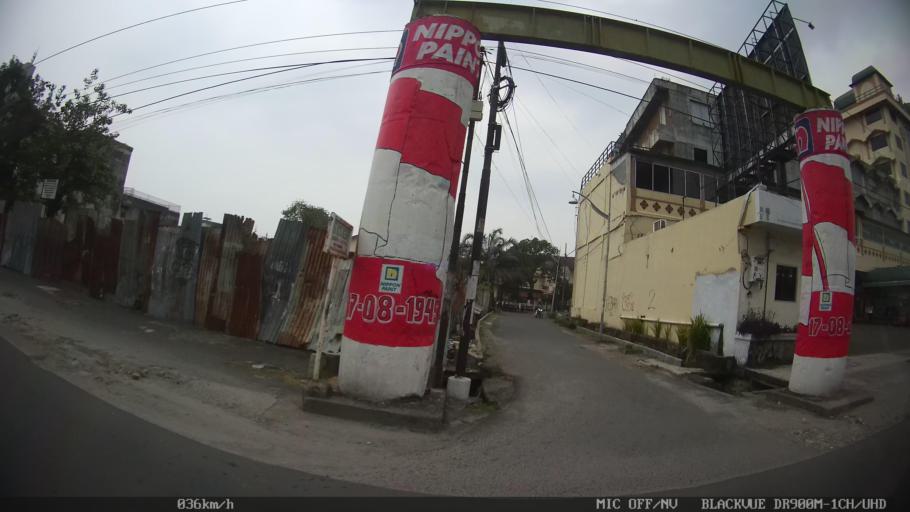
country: ID
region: North Sumatra
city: Medan
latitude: 3.5772
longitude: 98.6875
